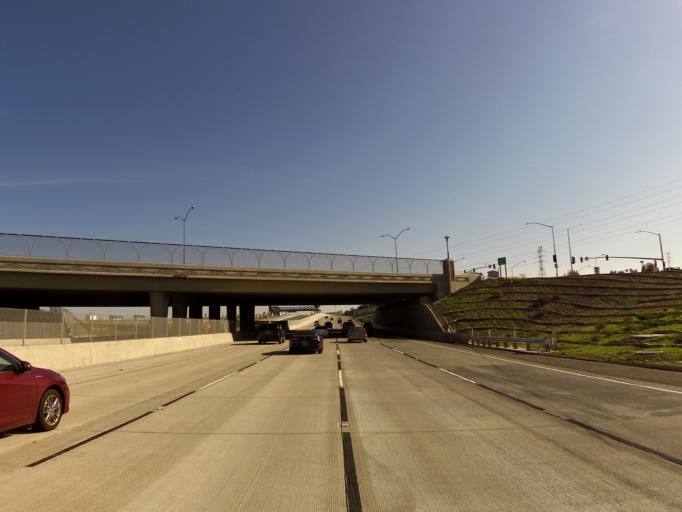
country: US
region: California
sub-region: Contra Costa County
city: Antioch
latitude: 37.9962
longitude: -121.7864
